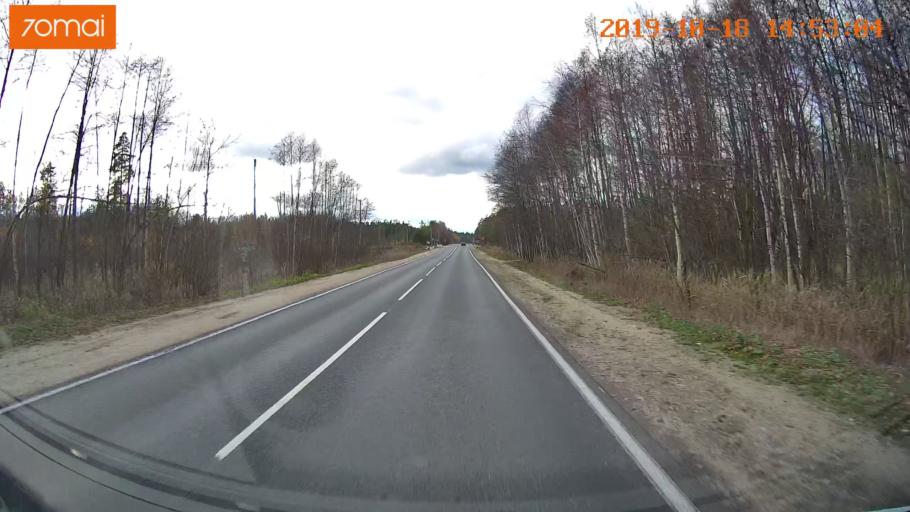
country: RU
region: Vladimir
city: Kurlovo
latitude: 55.4348
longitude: 40.6224
